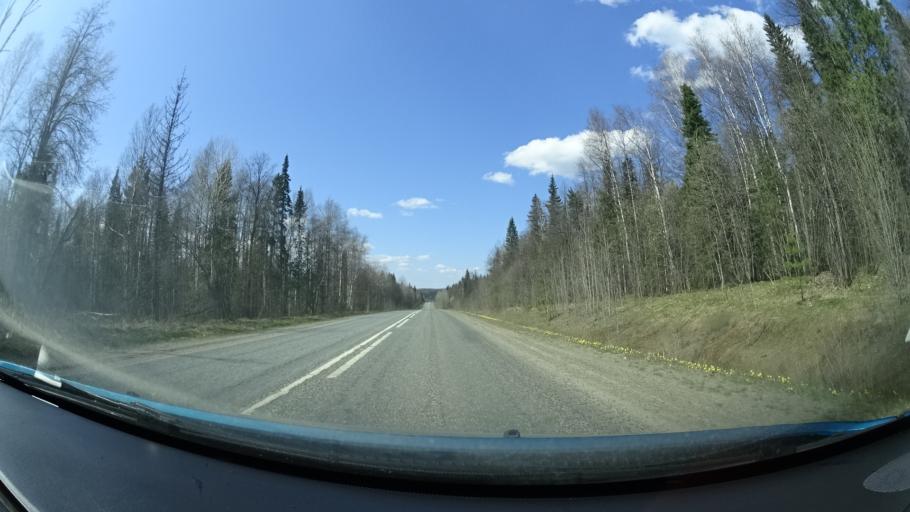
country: RU
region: Perm
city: Yugo-Kamskiy
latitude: 57.6077
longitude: 55.6497
